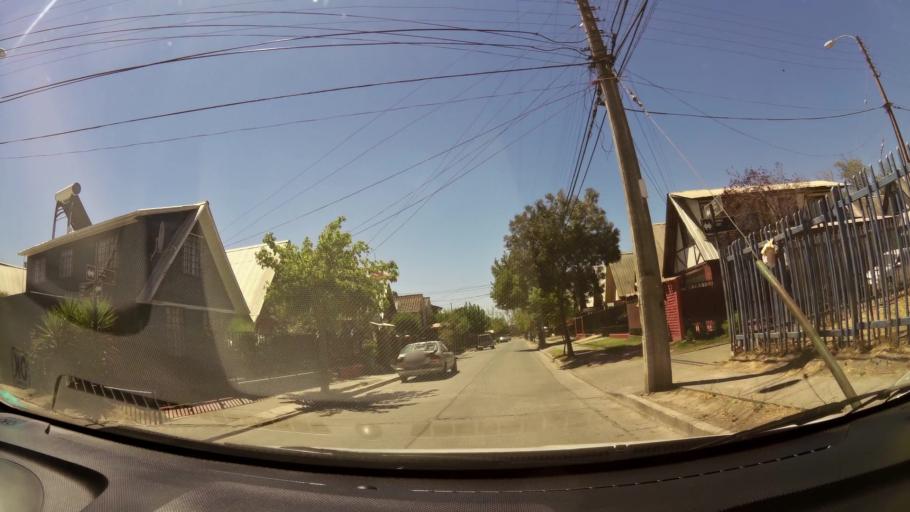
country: CL
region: O'Higgins
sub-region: Provincia de Cachapoal
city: Rancagua
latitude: -34.1657
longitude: -70.7645
